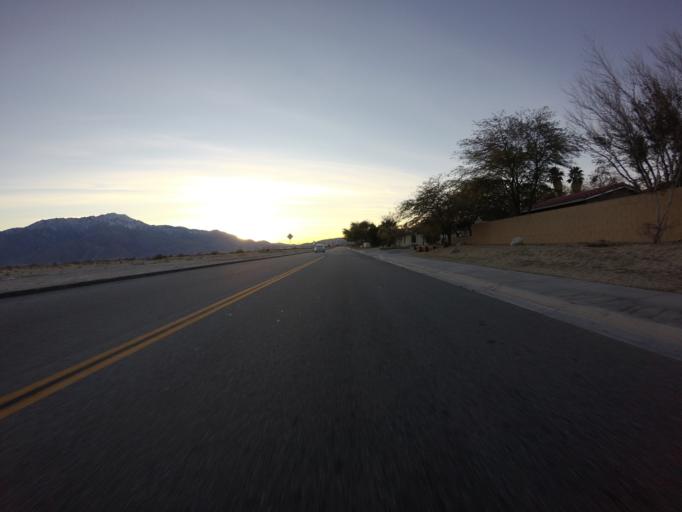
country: US
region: California
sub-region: Riverside County
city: Desert Hot Springs
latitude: 33.9469
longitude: -116.5118
